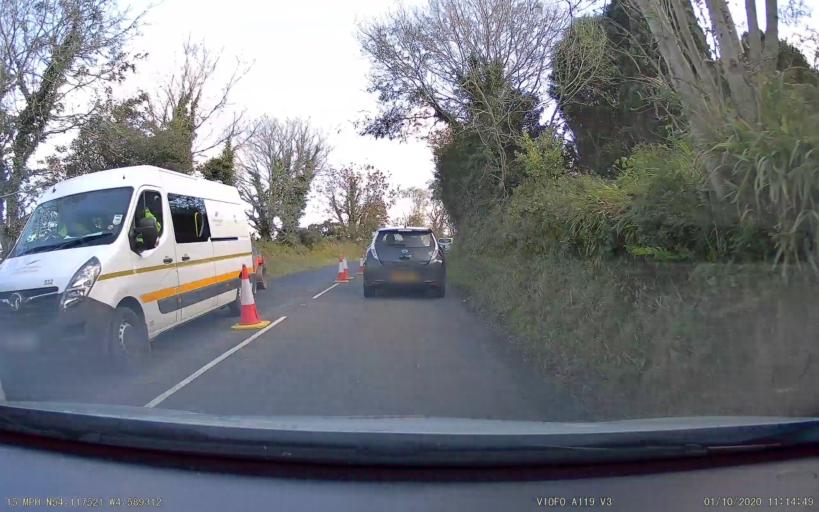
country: IM
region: Castletown
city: Castletown
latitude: 54.1175
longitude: -4.5893
